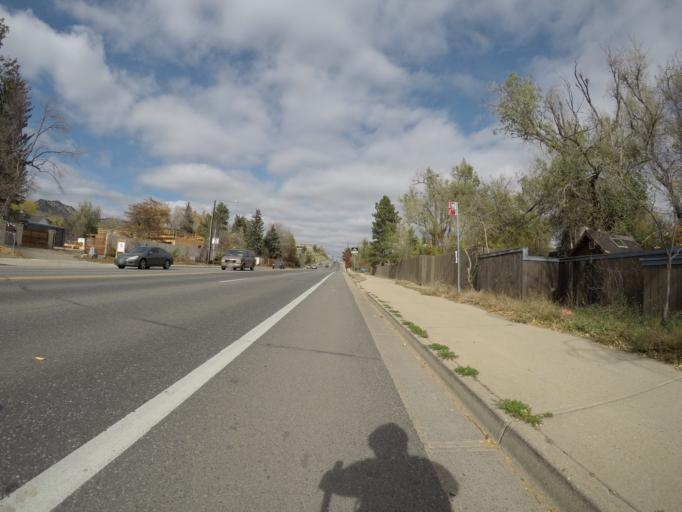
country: US
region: Colorado
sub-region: Boulder County
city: Boulder
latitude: 40.0393
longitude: -105.2820
